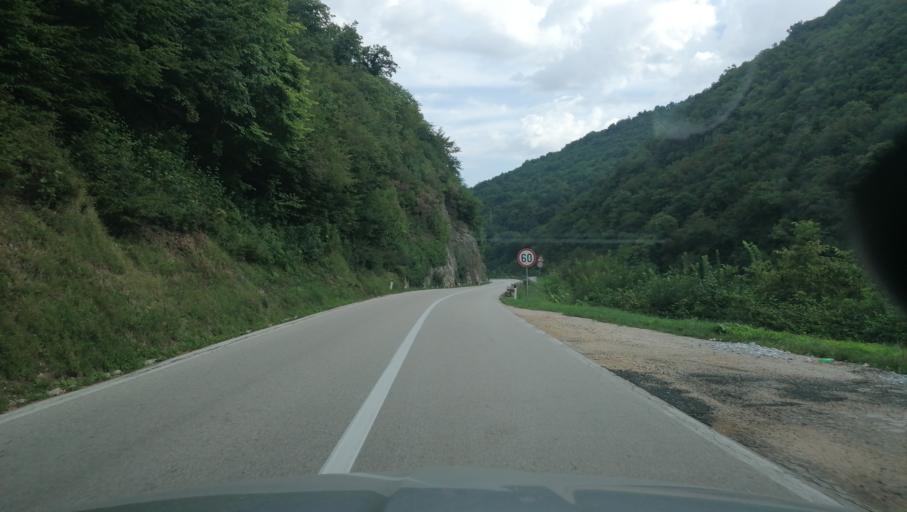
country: BA
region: Republika Srpska
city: Mrkonjic Grad
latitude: 44.5494
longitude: 17.1435
